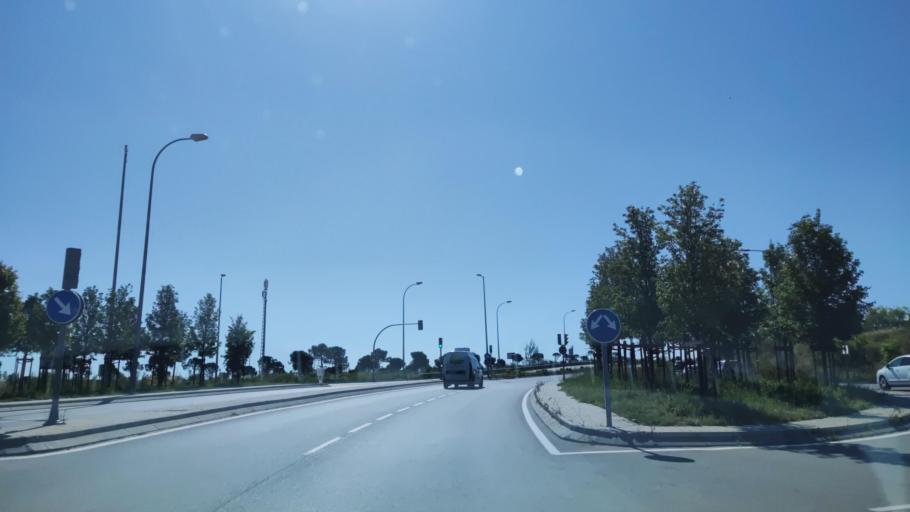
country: ES
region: Madrid
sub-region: Provincia de Madrid
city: San Blas
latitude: 40.4330
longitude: -3.6010
